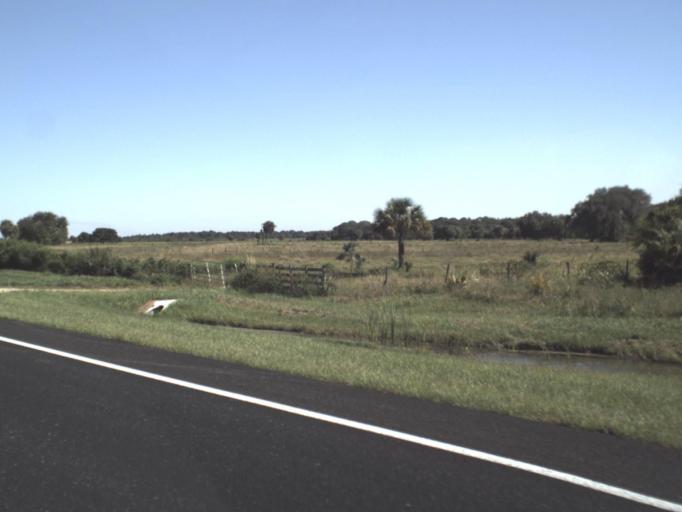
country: US
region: Florida
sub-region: Hendry County
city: Port LaBelle
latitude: 26.7683
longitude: -81.3123
